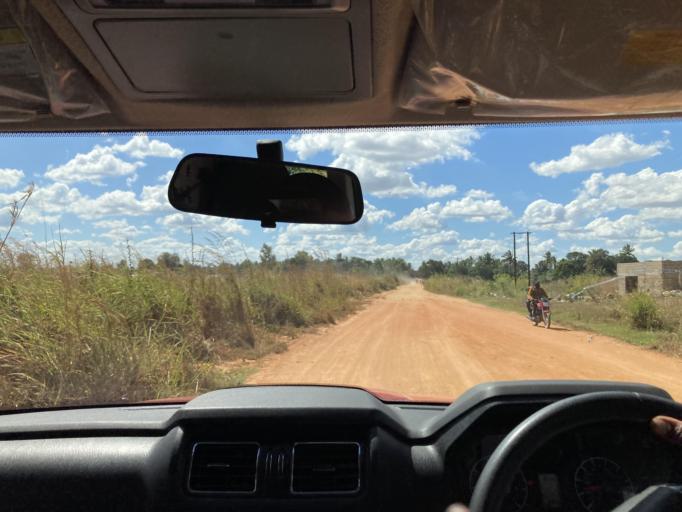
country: MZ
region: Cabo Delgado
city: Montepuez
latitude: -13.1481
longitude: 38.9916
